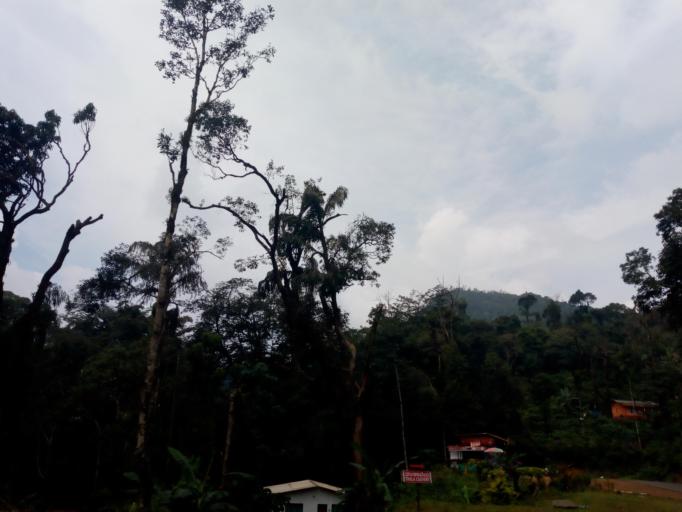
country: IN
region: Karnataka
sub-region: Dakshina Kannada
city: Sulya
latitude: 12.3811
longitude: 75.5131
